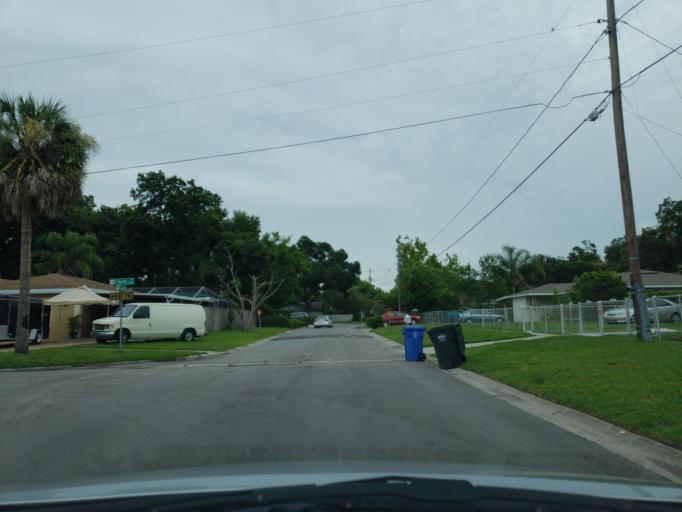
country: US
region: Florida
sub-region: Hillsborough County
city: Egypt Lake-Leto
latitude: 28.0054
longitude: -82.4916
